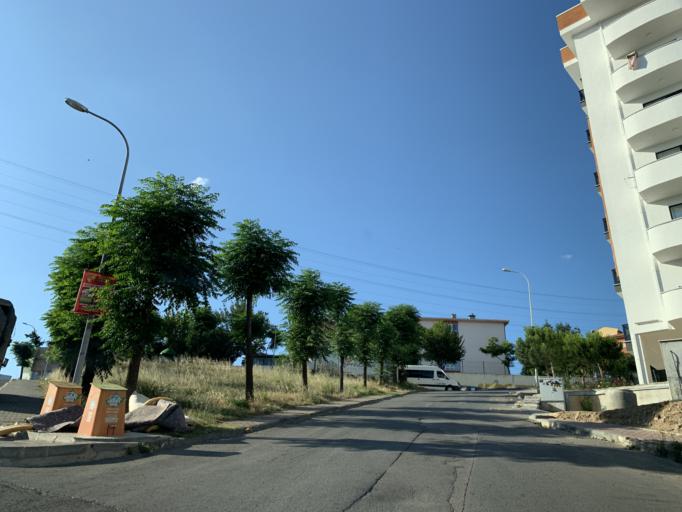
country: TR
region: Istanbul
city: Pendik
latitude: 40.8967
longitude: 29.2452
